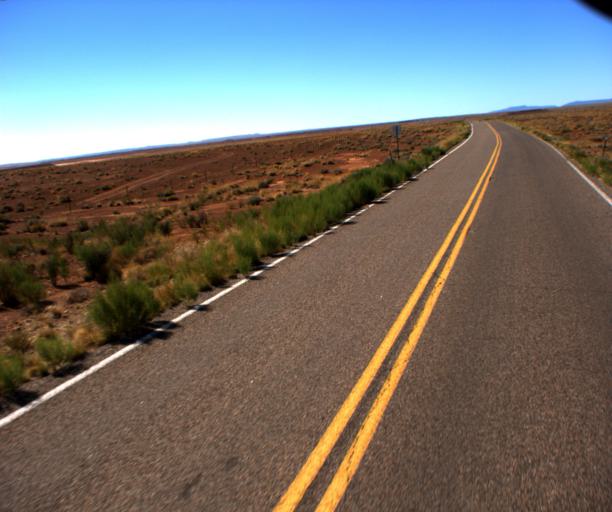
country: US
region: Arizona
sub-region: Coconino County
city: LeChee
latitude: 35.2408
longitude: -110.9602
